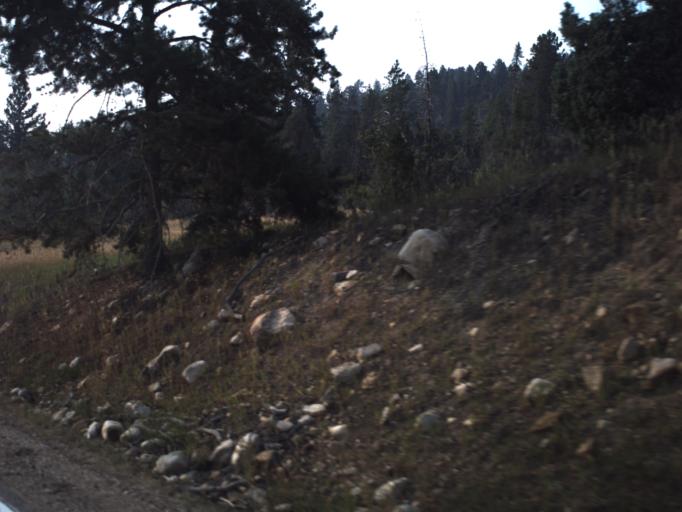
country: US
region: Utah
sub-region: Summit County
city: Francis
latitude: 40.6005
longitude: -111.1073
